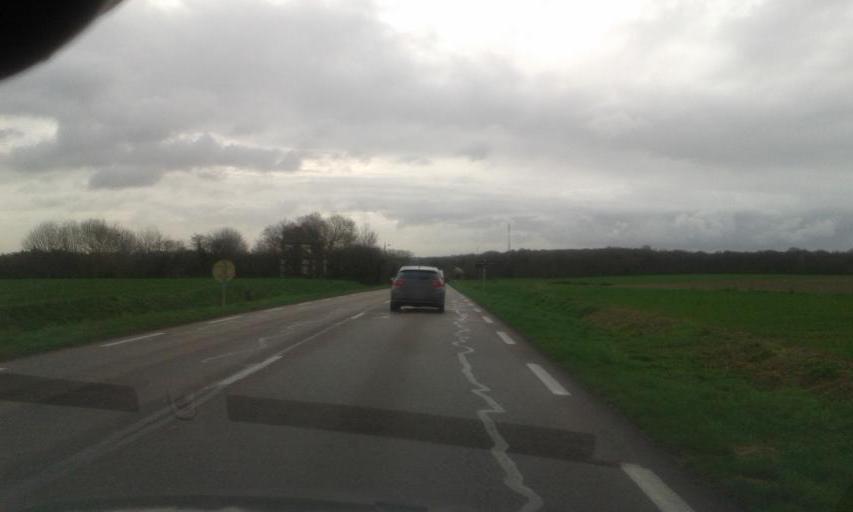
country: FR
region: Haute-Normandie
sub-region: Departement de l'Eure
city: Fleury-sur-Andelle
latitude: 49.3769
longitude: 1.3268
